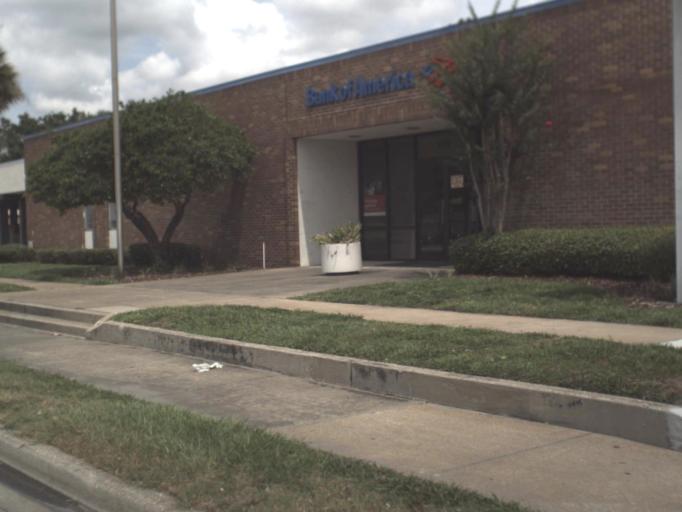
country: US
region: Florida
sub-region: Duval County
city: Jacksonville
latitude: 30.4300
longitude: -81.6629
